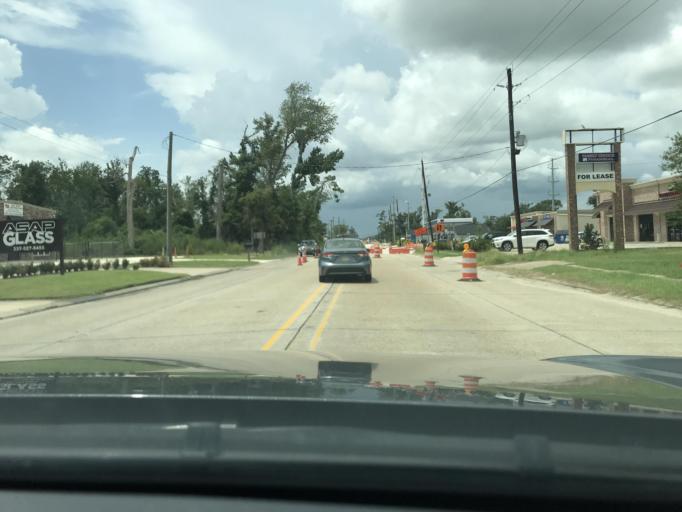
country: US
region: Louisiana
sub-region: Calcasieu Parish
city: Sulphur
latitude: 30.2276
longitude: -93.3377
